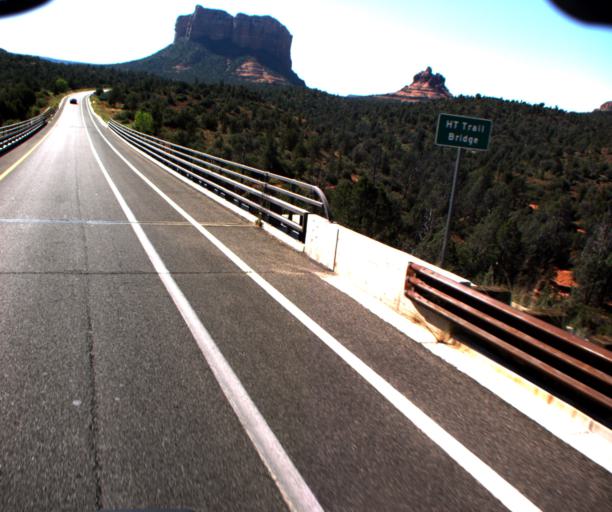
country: US
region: Arizona
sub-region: Yavapai County
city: Village of Oak Creek (Big Park)
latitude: 34.8196
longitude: -111.7745
